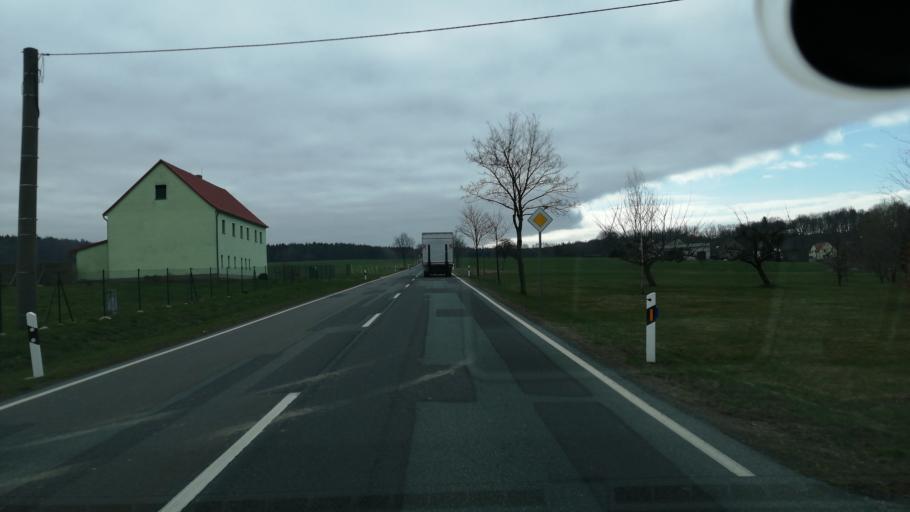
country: DE
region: Saxony
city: Niedercunnersdorf
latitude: 51.0581
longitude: 14.6959
